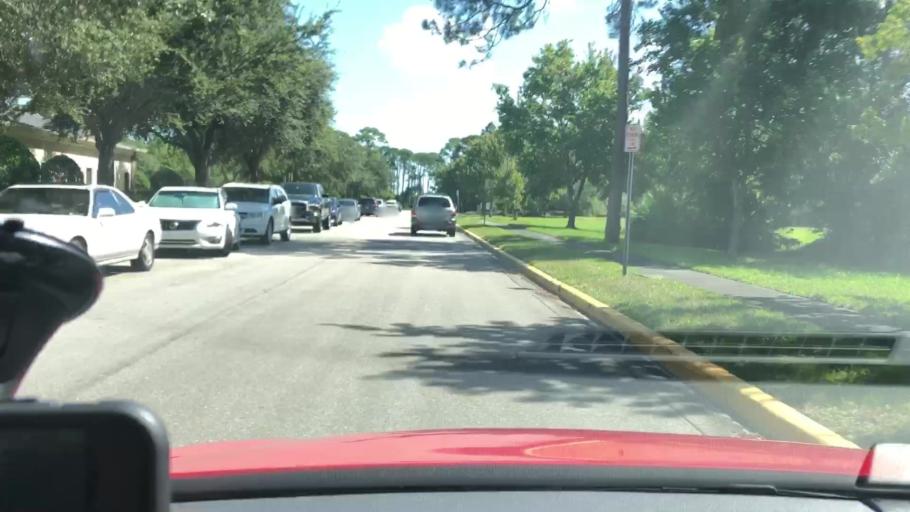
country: US
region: Florida
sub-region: Volusia County
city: Daytona Beach
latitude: 29.2065
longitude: -81.0625
